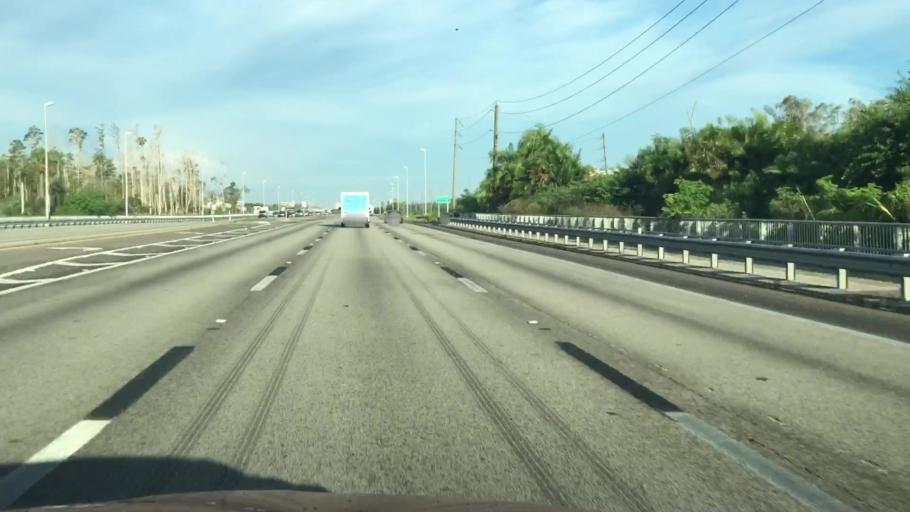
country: US
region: Florida
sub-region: Lee County
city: Tice
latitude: 26.6289
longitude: -81.7872
